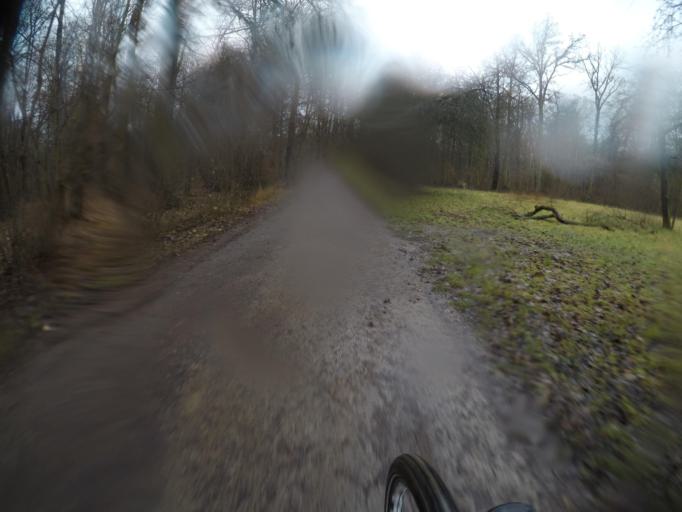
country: DE
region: Baden-Wuerttemberg
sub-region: Regierungsbezirk Stuttgart
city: Pleidelsheim
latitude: 48.9493
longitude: 9.1657
